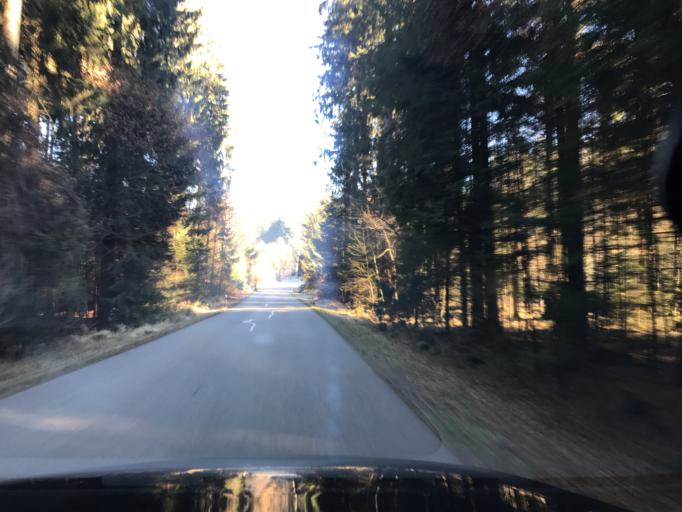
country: DE
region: Bavaria
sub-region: Upper Bavaria
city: Prutting
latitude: 47.8898
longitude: 12.1640
